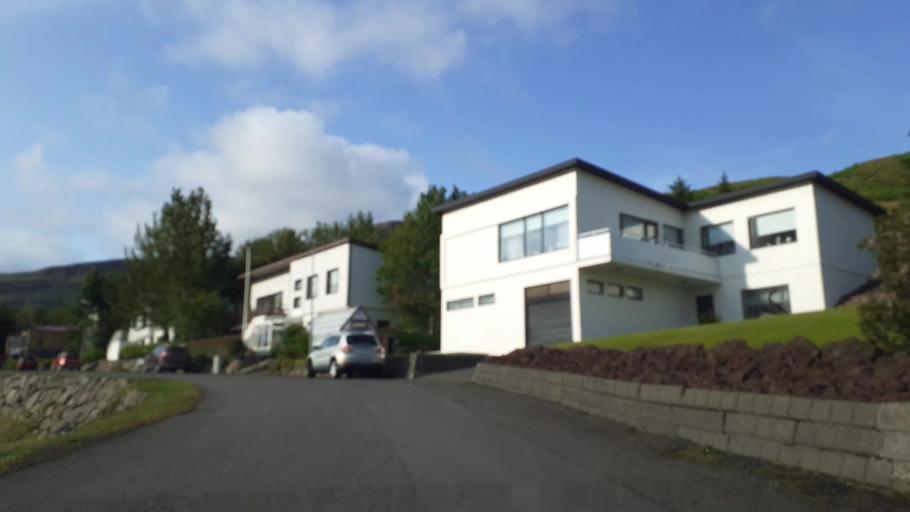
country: IS
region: East
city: Eskifjoerdur
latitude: 65.0663
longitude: -14.0026
